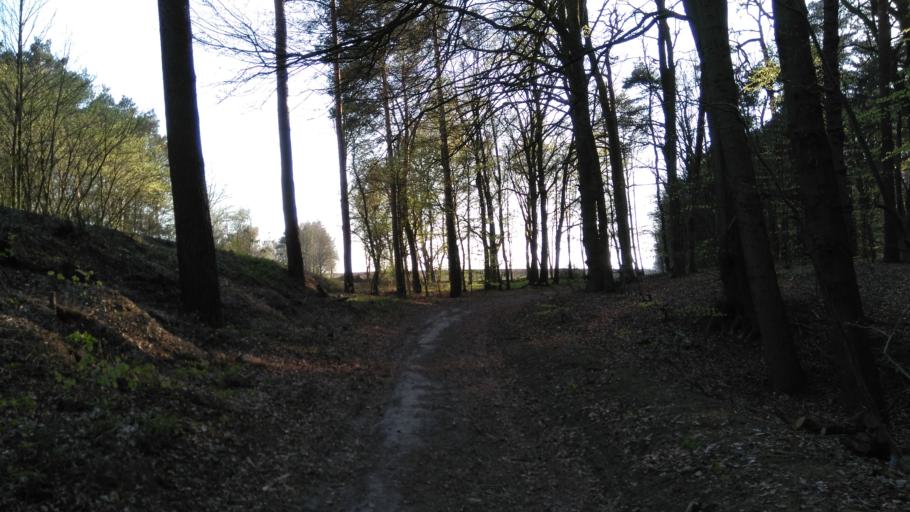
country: DE
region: Lower Saxony
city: Buxtehude
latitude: 53.4693
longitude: 9.6582
